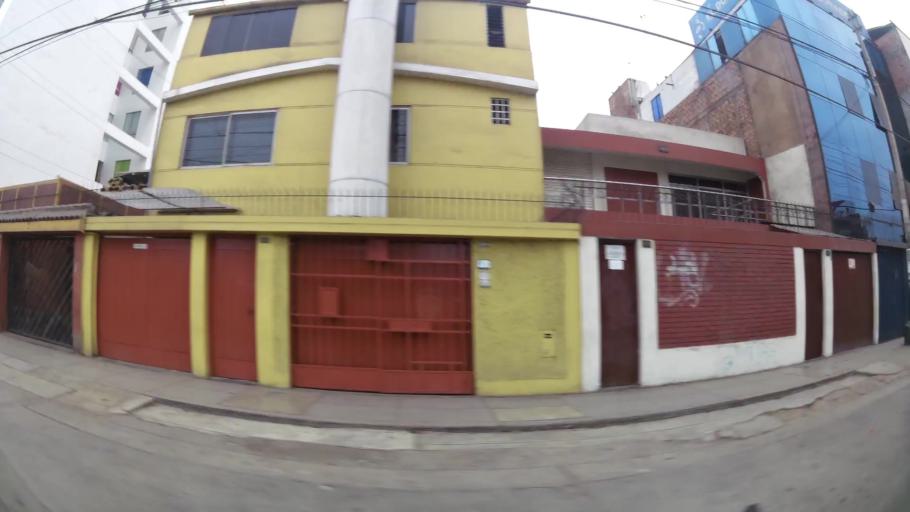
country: PE
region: Callao
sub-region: Callao
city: Callao
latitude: -12.0568
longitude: -77.0978
